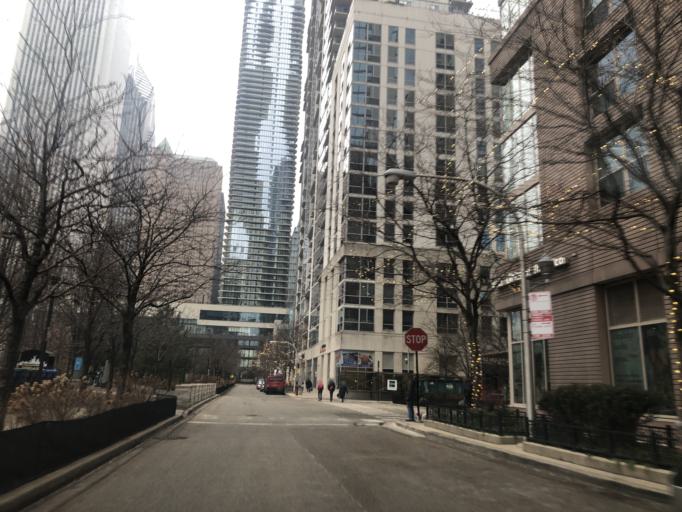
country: US
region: Illinois
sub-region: Cook County
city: Chicago
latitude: 41.8865
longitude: -87.6169
